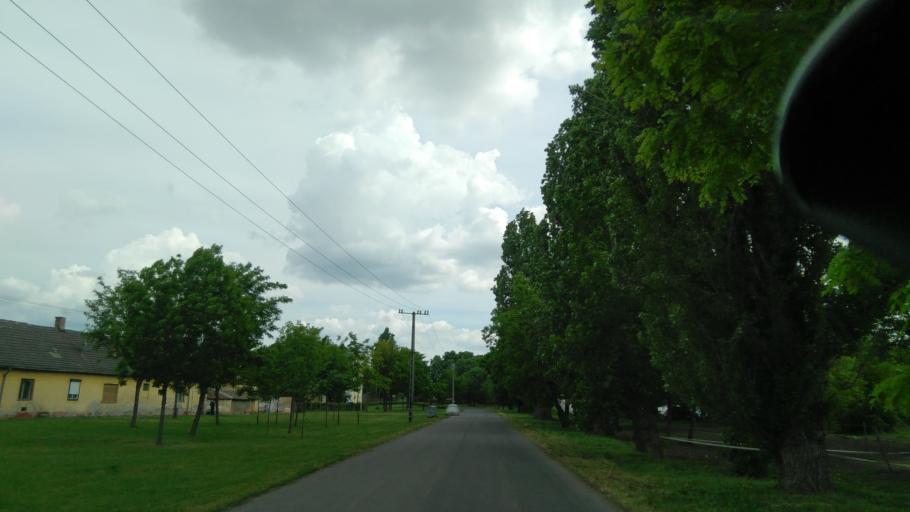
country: HU
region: Bekes
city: Mezohegyes
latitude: 46.3165
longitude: 20.8210
